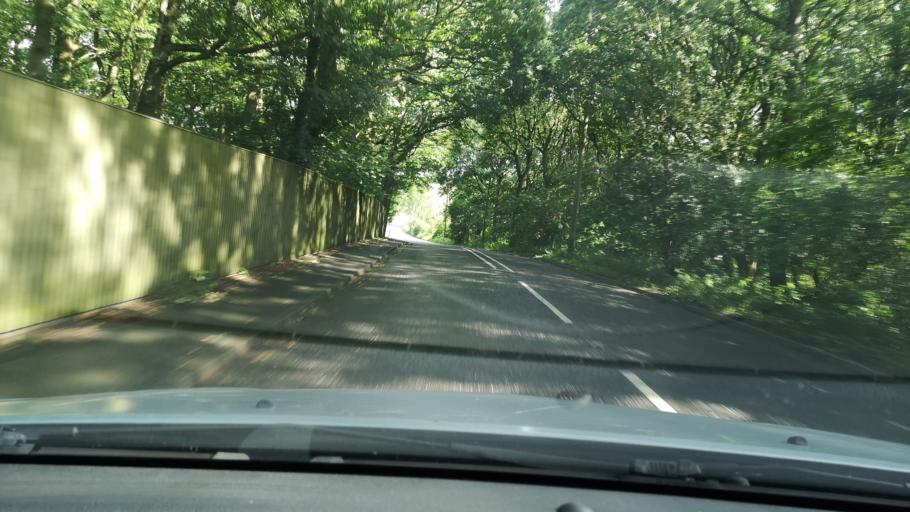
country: GB
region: England
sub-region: City and Borough of Wakefield
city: Ossett
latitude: 53.7094
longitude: -1.5646
